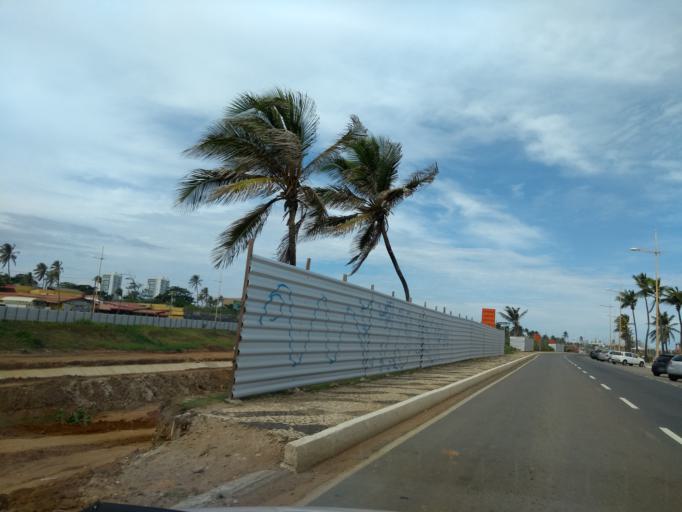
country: BR
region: Bahia
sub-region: Lauro De Freitas
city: Lauro de Freitas
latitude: -12.9583
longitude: -38.3918
